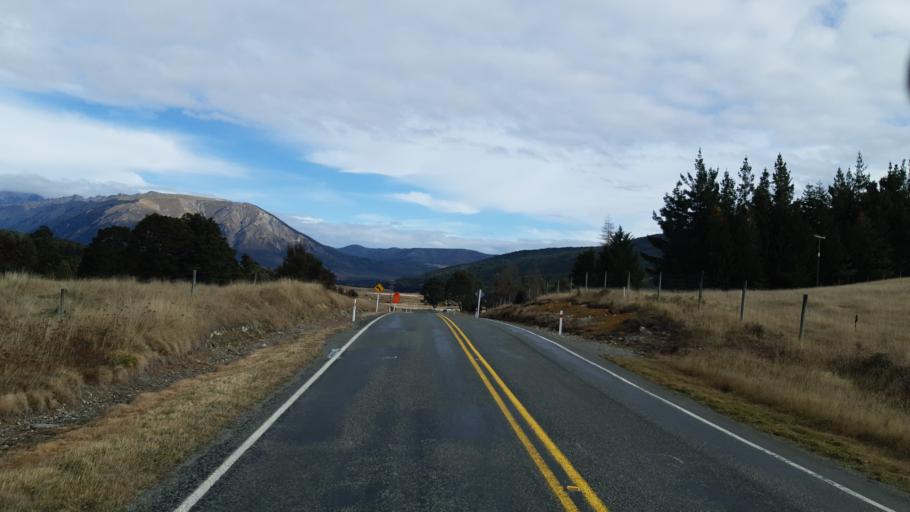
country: NZ
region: Tasman
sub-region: Tasman District
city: Wakefield
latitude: -41.7872
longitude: 172.8881
